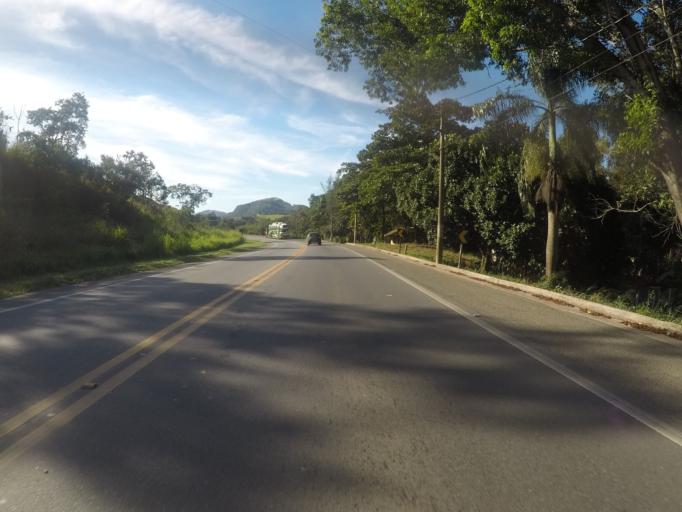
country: BR
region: Espirito Santo
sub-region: Fundao
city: Fundao
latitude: -19.9290
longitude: -40.4059
